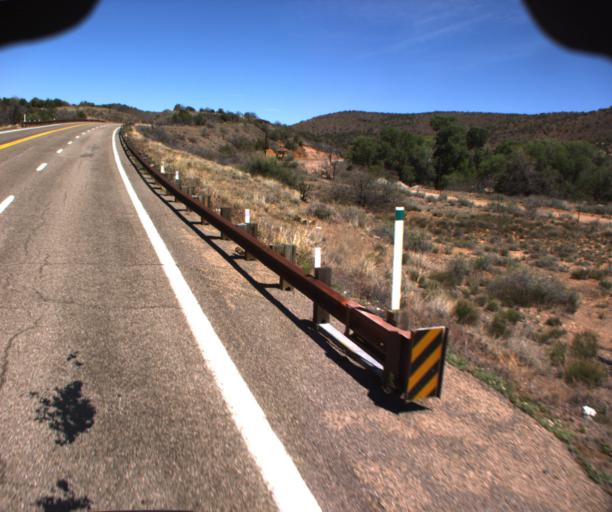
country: US
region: Arizona
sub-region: Mohave County
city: Peach Springs
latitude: 35.4305
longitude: -113.6492
